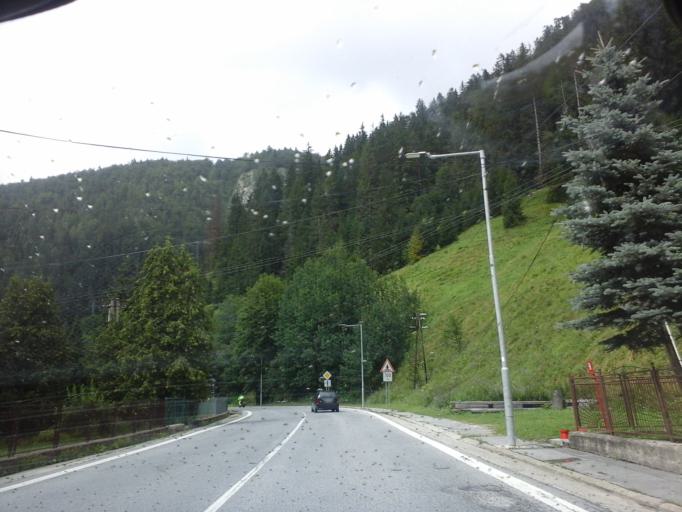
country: SK
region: Kosicky
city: Dobsina
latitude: 48.8701
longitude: 20.3431
